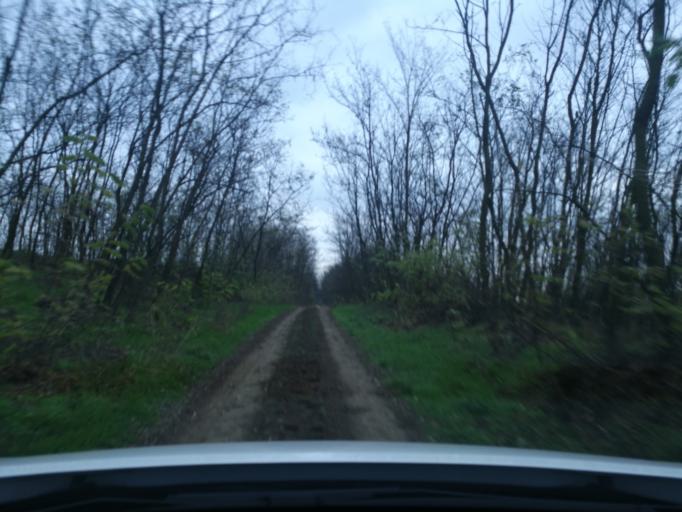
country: HU
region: Szabolcs-Szatmar-Bereg
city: Nyirpazony
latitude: 47.9700
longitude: 21.7851
